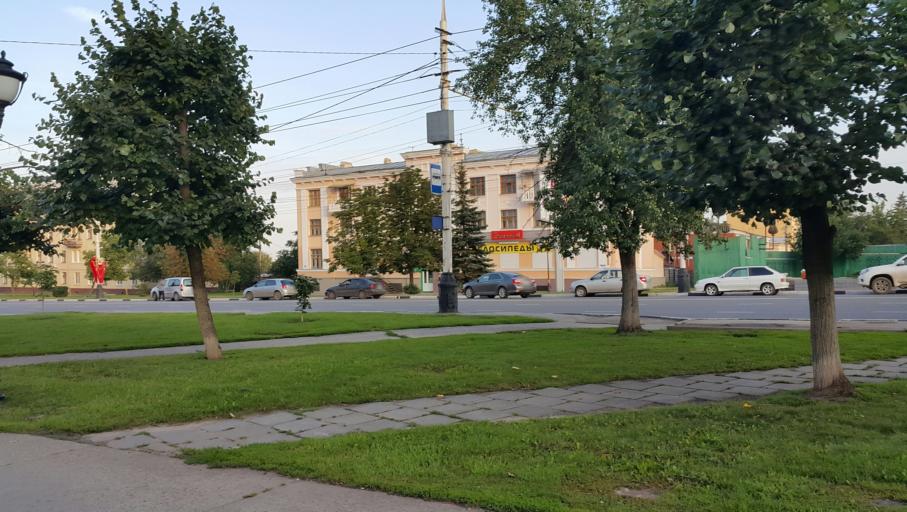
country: RU
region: Tambov
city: Tambov
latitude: 52.7194
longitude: 41.4306
